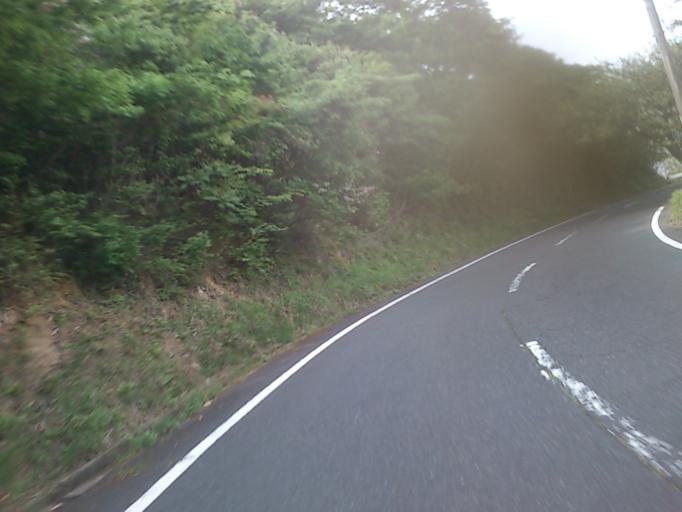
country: JP
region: Hyogo
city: Toyooka
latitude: 35.6904
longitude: 134.9865
